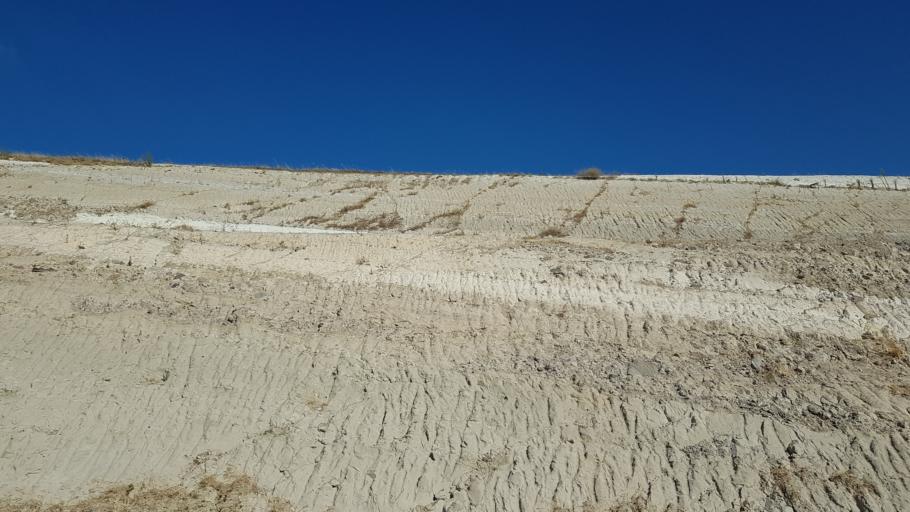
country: TR
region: Balikesir
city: Ertugrul
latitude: 39.5467
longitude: 27.6804
